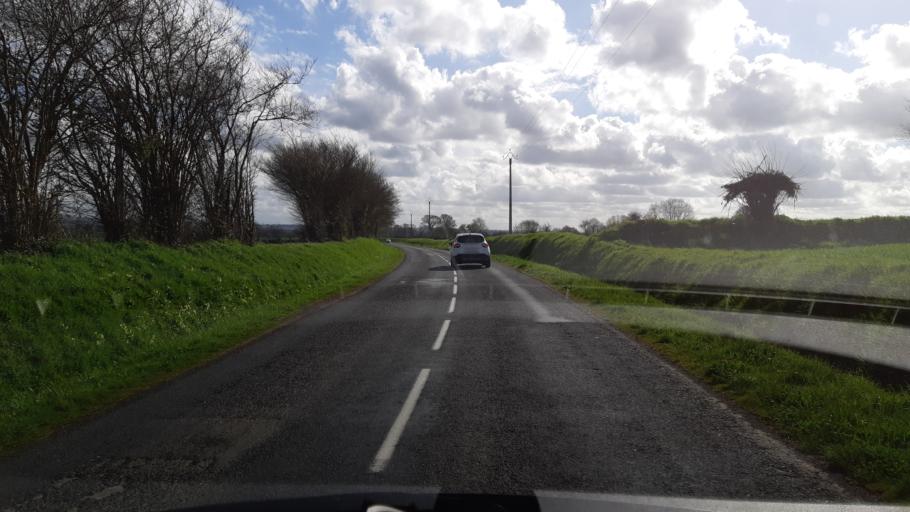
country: FR
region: Lower Normandy
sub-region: Departement de la Manche
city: Percy
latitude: 49.0222
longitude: -1.1592
